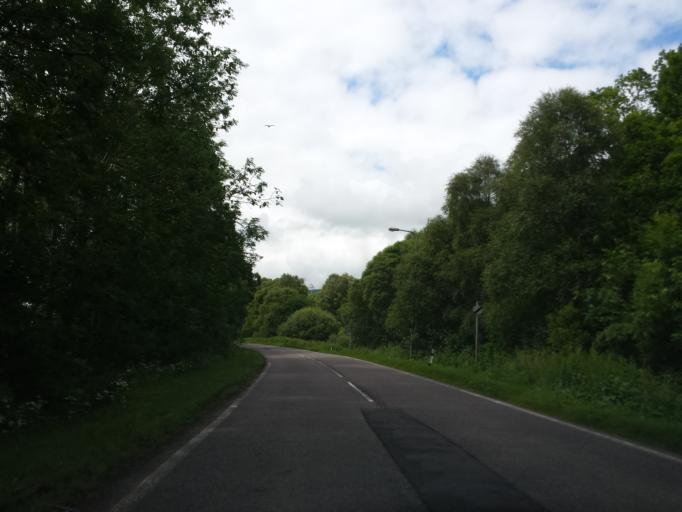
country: GB
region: Scotland
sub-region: Highland
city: Fort William
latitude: 56.8455
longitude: -5.1523
